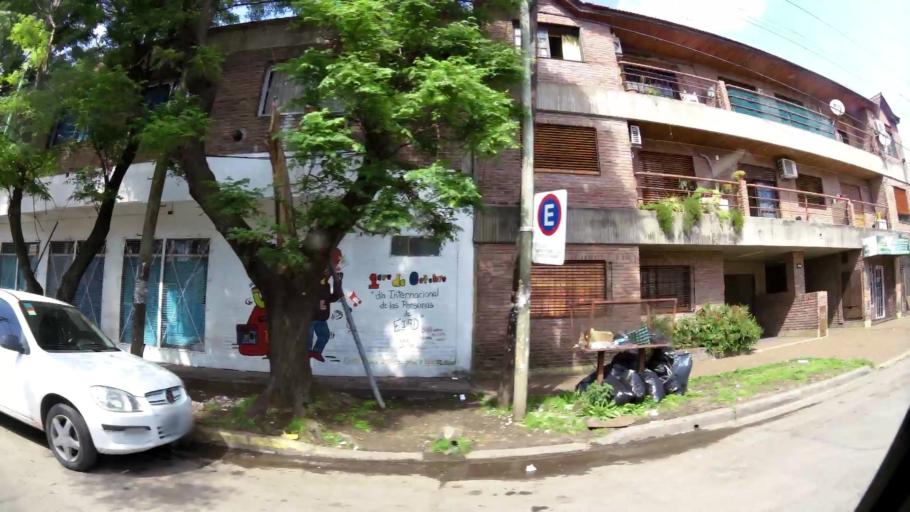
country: AR
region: Buenos Aires
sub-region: Partido de Quilmes
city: Quilmes
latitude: -34.8061
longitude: -58.2731
